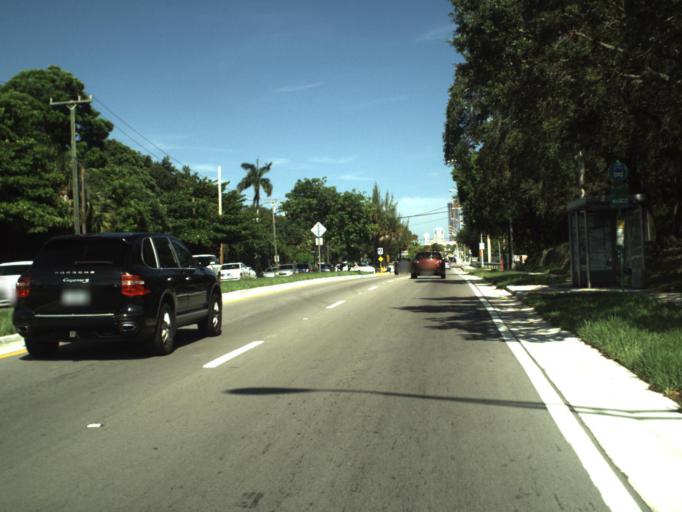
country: US
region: Florida
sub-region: Miami-Dade County
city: Ojus
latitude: 25.9471
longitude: -80.1565
